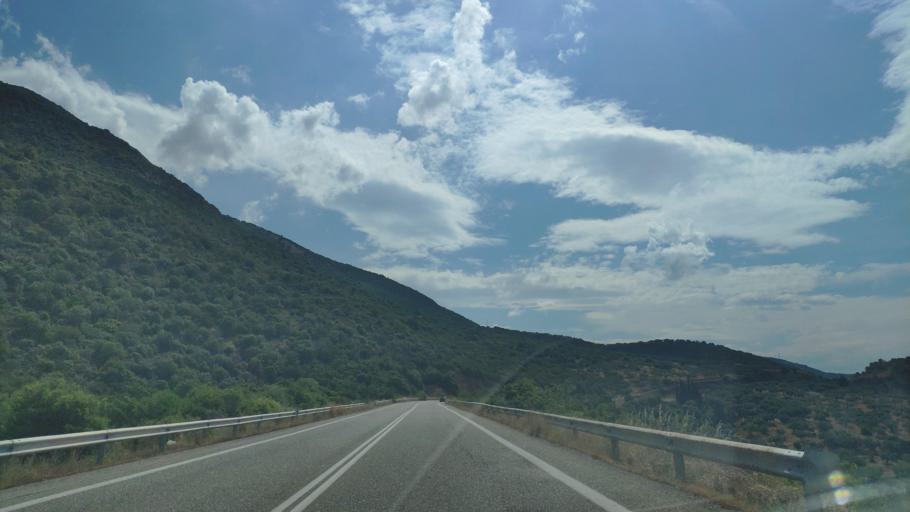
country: GR
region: West Greece
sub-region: Nomos Achaias
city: Kamarai
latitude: 38.3931
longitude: 22.0675
